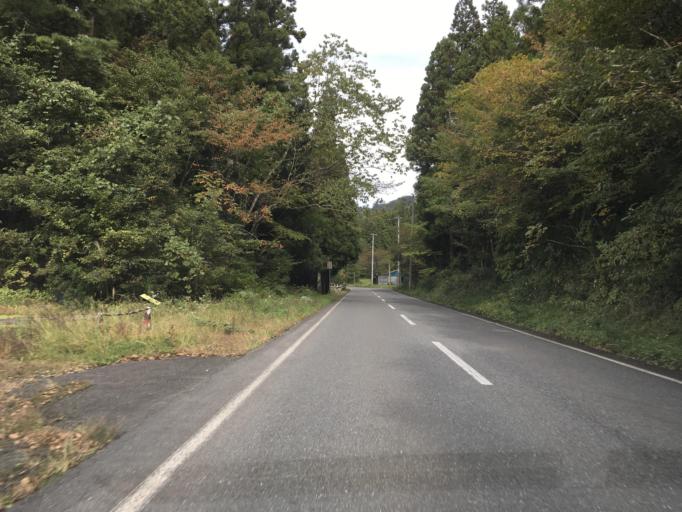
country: JP
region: Iwate
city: Mizusawa
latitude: 39.0375
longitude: 141.3006
